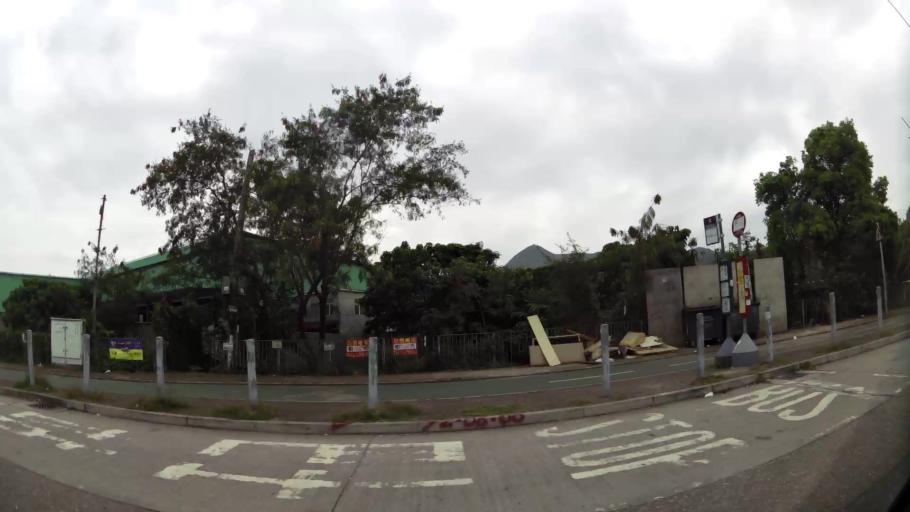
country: HK
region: Yuen Long
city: Yuen Long Kau Hui
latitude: 22.4365
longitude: 113.9919
